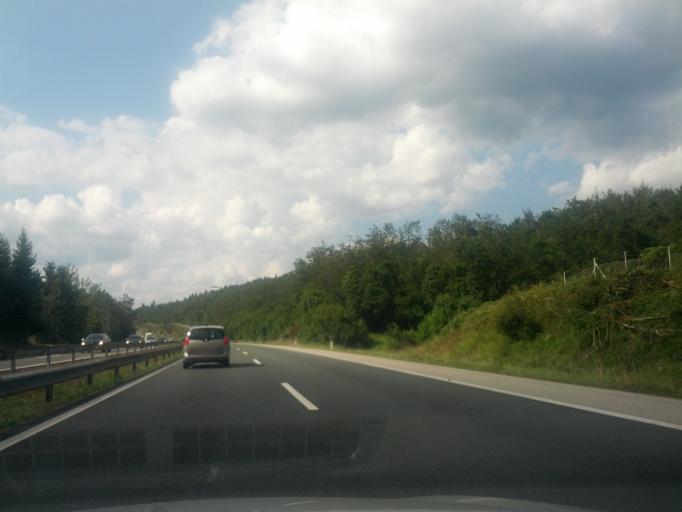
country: SI
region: Cerknica
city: Rakek
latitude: 45.8408
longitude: 14.2934
